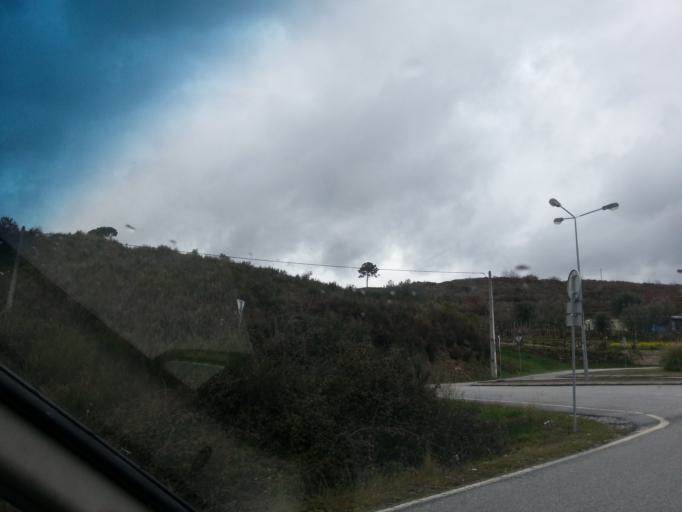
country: PT
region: Viseu
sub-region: Viseu
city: Rio de Loba
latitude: 40.6097
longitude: -7.8654
